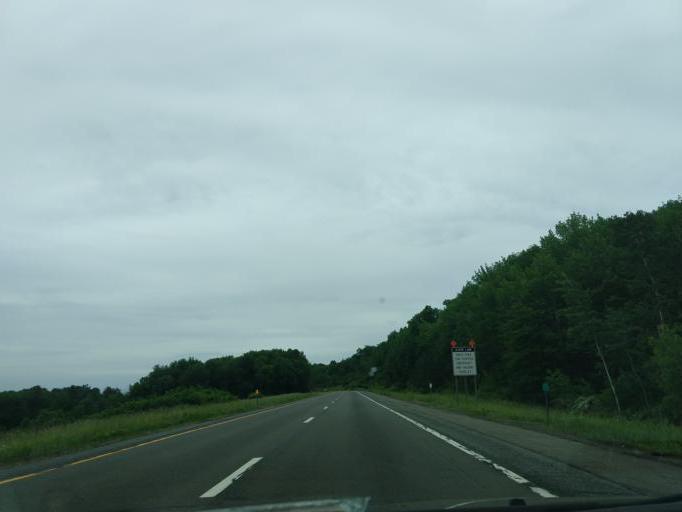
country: US
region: New York
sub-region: Broome County
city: Chenango Bridge
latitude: 42.2853
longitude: -75.9267
